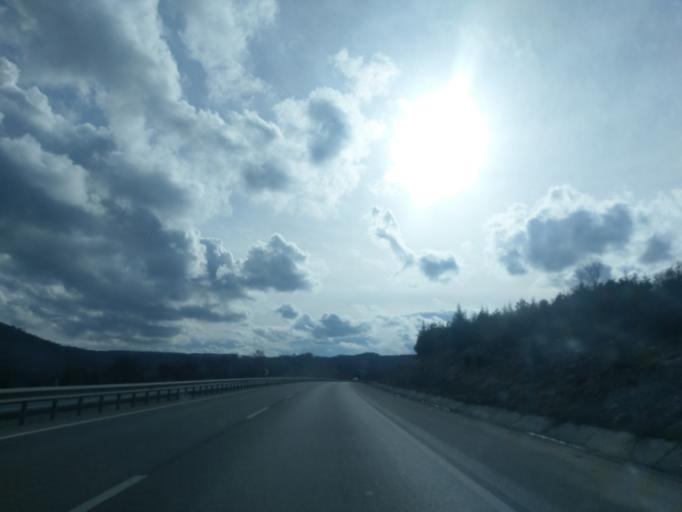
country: TR
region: Kuetahya
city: Sabuncu
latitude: 39.5971
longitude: 30.1442
